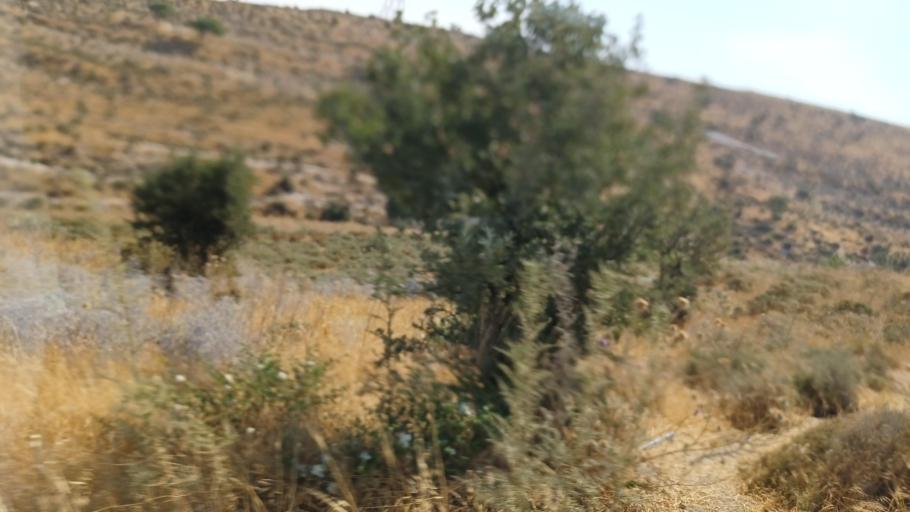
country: CY
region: Lefkosia
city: Lympia
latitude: 34.9847
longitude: 33.4796
